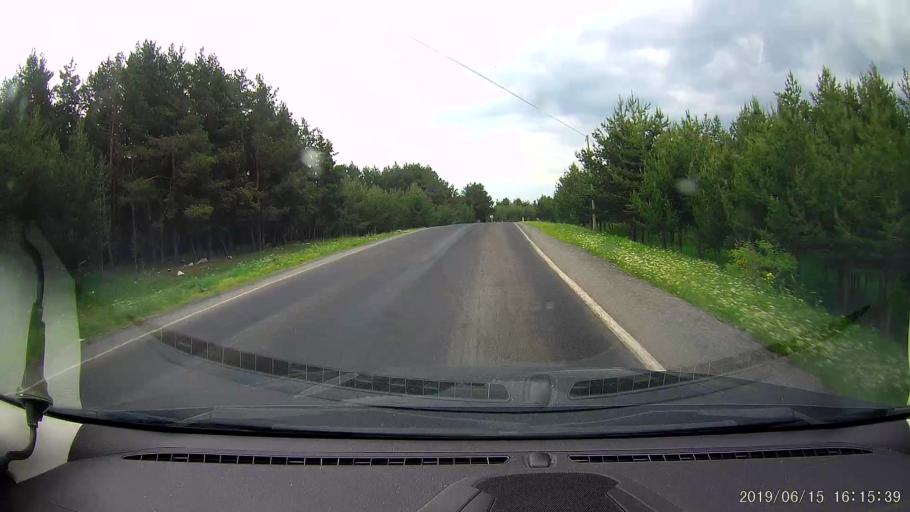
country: TR
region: Ardahan
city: Hanak
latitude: 41.2658
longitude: 42.8564
